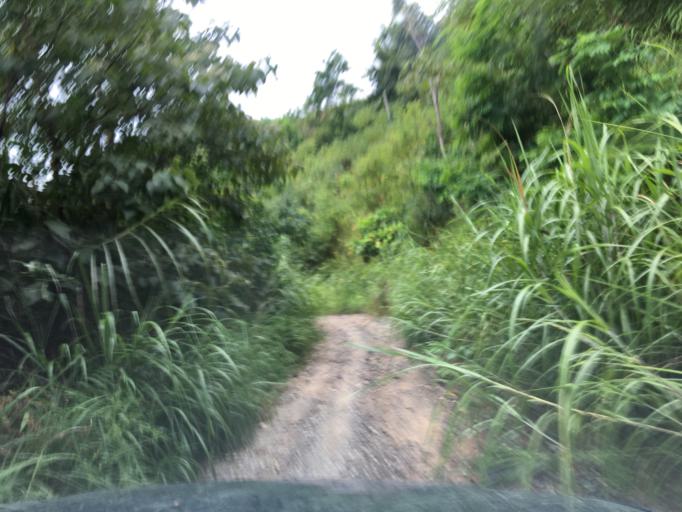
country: CN
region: Guangxi Zhuangzu Zizhiqu
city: Tongle
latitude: 25.0046
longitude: 105.9861
